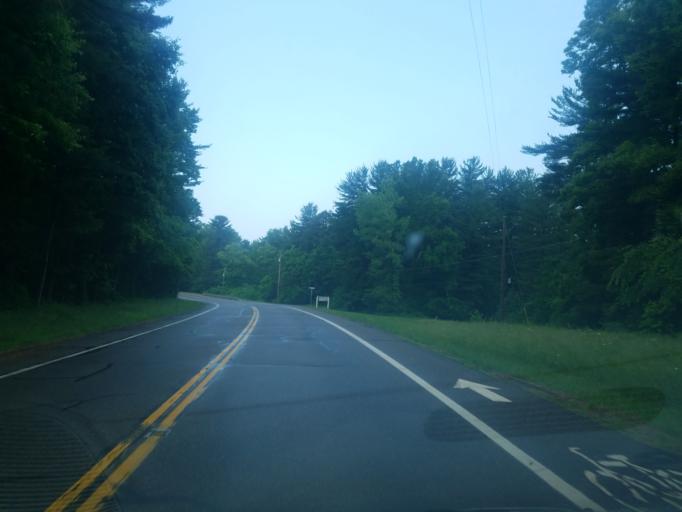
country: US
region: Ohio
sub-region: Tuscarawas County
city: Rockford
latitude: 40.5521
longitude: -81.2283
